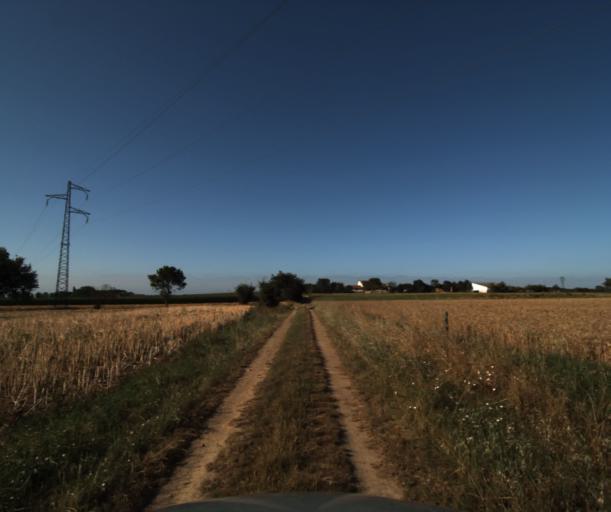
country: FR
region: Midi-Pyrenees
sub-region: Departement de la Haute-Garonne
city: Labarthe-sur-Leze
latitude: 43.4477
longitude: 1.3769
